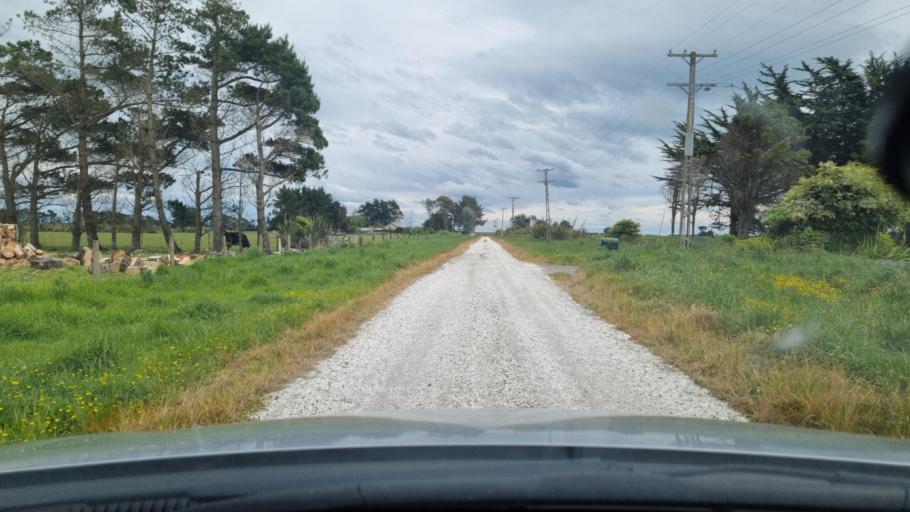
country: NZ
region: Southland
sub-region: Invercargill City
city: Invercargill
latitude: -46.3914
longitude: 168.2959
